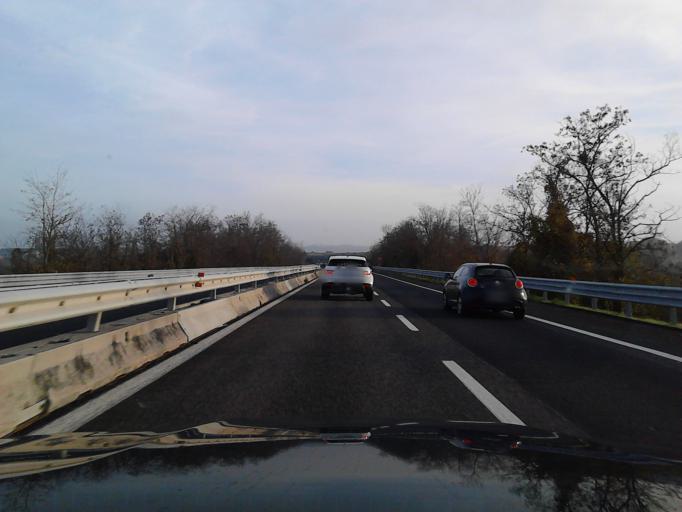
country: IT
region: Abruzzo
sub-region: Provincia di Chieti
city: Ortona
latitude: 42.3204
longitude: 14.3981
